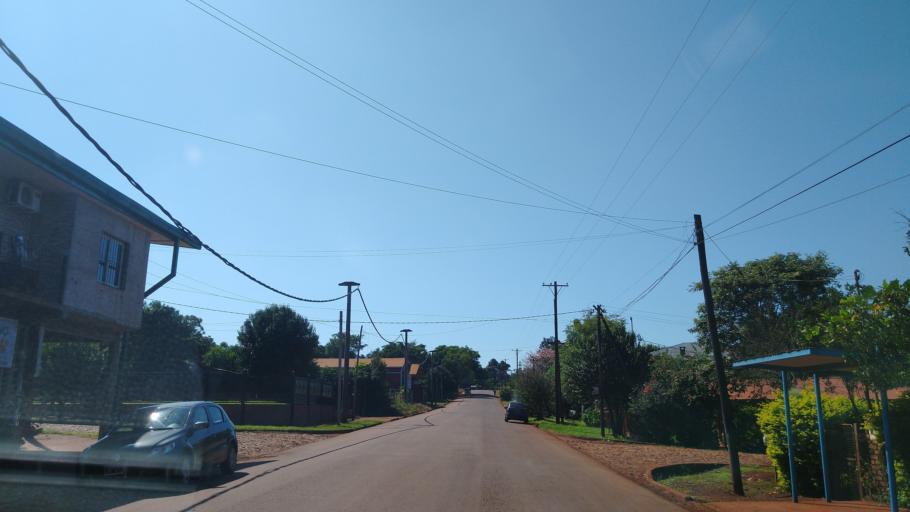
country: AR
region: Misiones
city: Puerto Libertad
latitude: -25.9770
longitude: -54.5748
